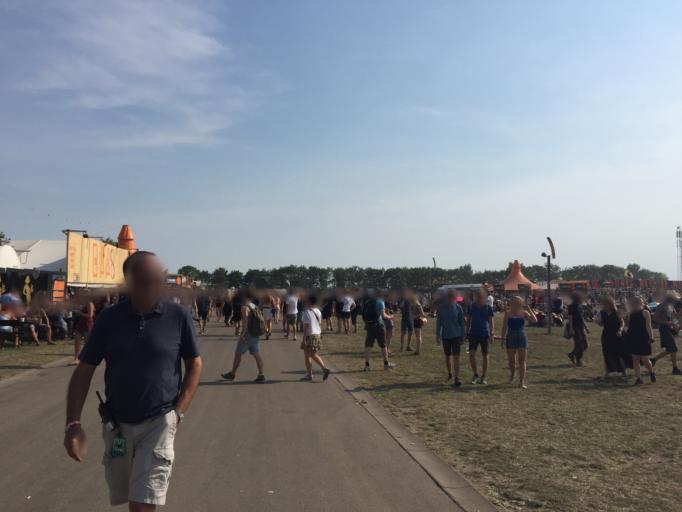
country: DK
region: Zealand
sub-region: Roskilde Kommune
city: Roskilde
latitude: 55.6212
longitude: 12.0790
